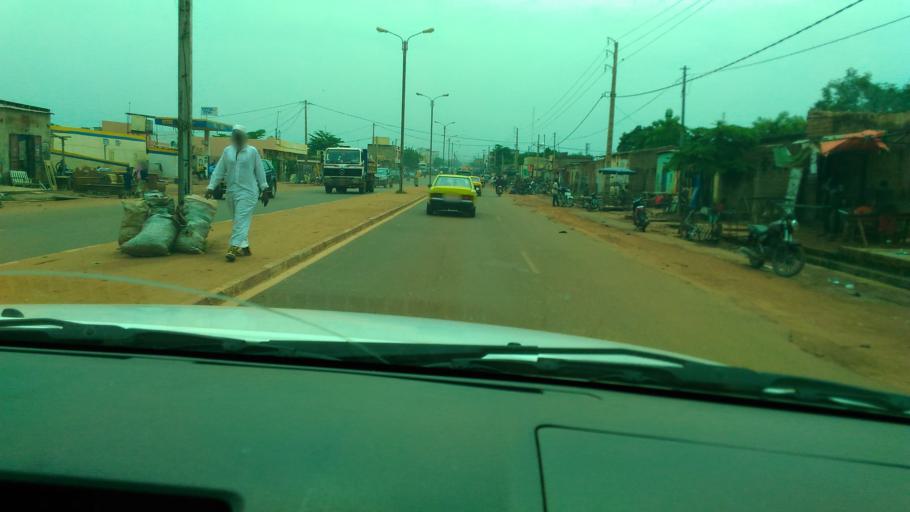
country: ML
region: Bamako
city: Bamako
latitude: 12.5728
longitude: -7.9721
